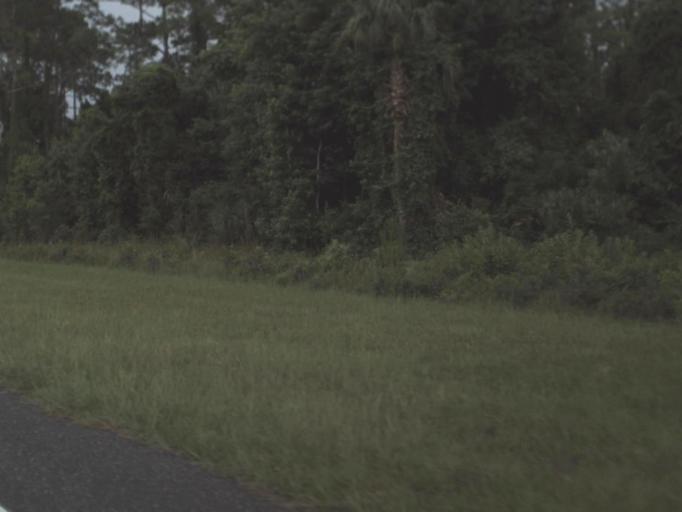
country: US
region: Florida
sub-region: Levy County
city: Inglis
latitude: 29.1690
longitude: -82.6477
